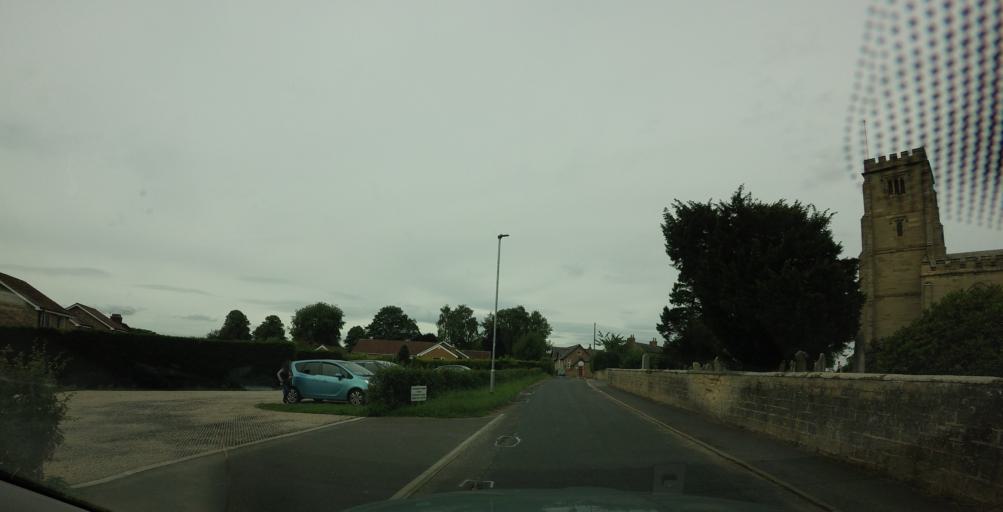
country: GB
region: England
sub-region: North Yorkshire
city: Ripon
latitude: 54.1432
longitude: -1.5002
